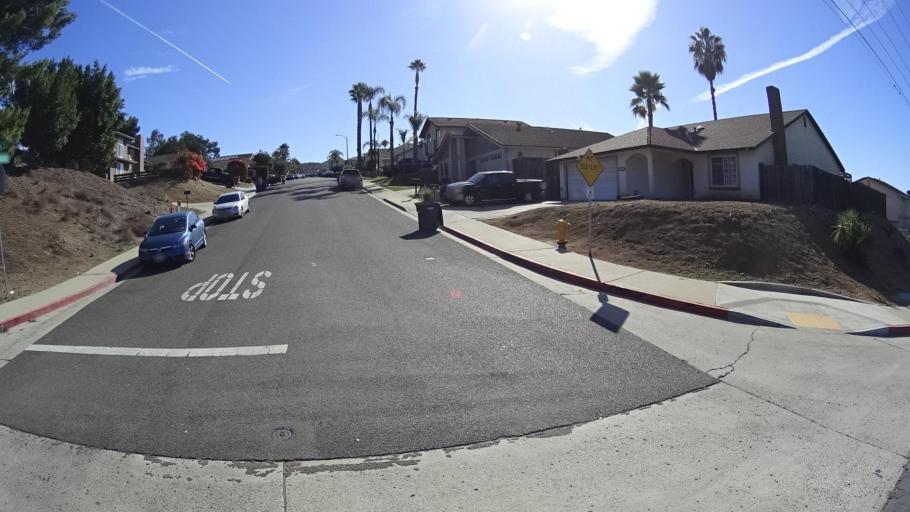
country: US
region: California
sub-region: San Diego County
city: Granite Hills
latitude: 32.8208
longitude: -116.9141
